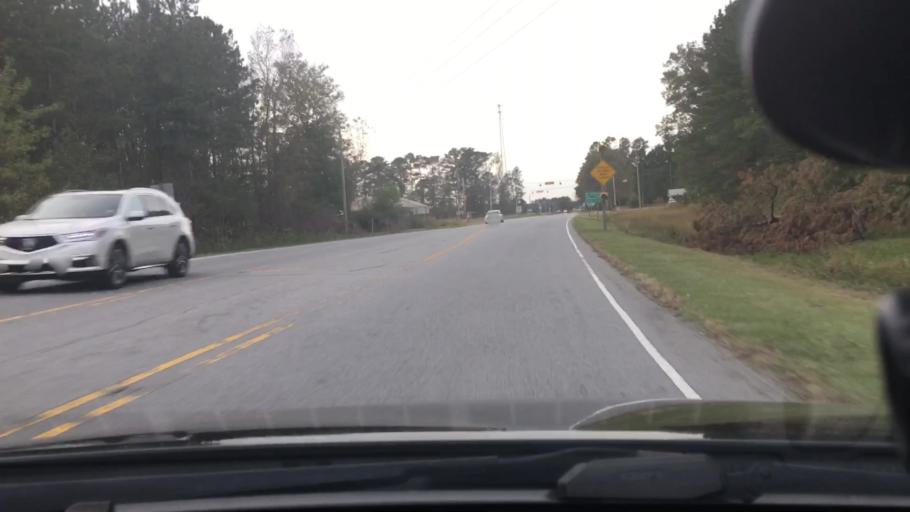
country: US
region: North Carolina
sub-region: Craven County
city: Vanceboro
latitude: 35.4170
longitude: -77.2553
